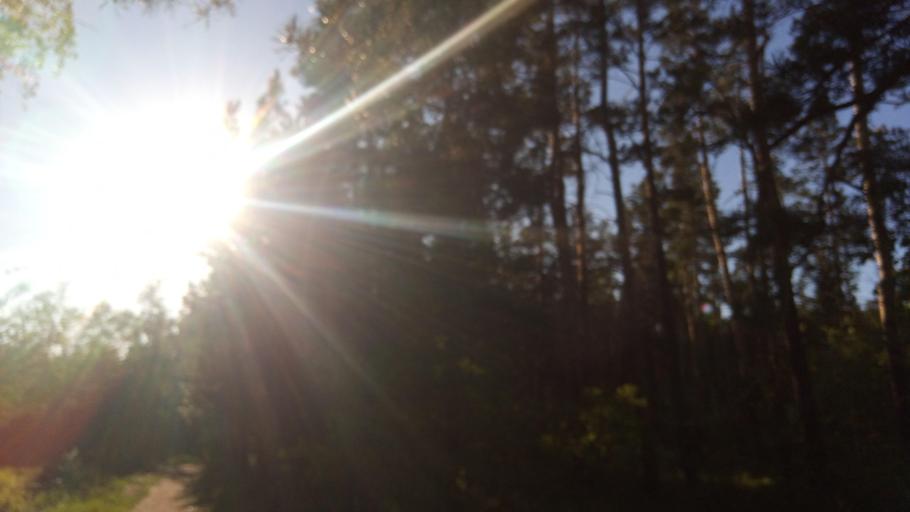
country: RU
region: Chelyabinsk
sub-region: Gorod Chelyabinsk
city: Chelyabinsk
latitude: 55.1267
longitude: 61.3425
